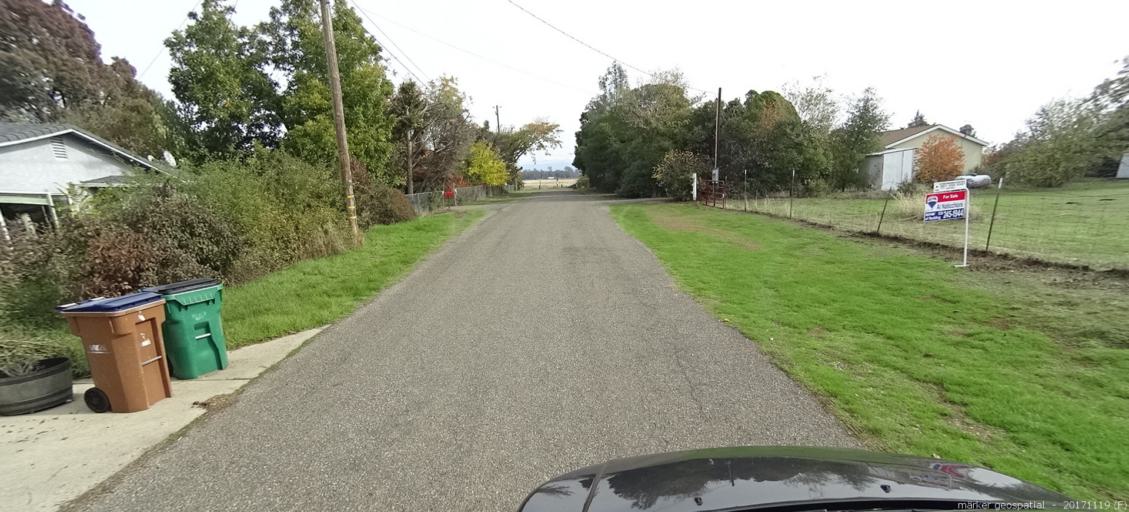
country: US
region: California
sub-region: Shasta County
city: Anderson
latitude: 40.4869
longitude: -122.2853
